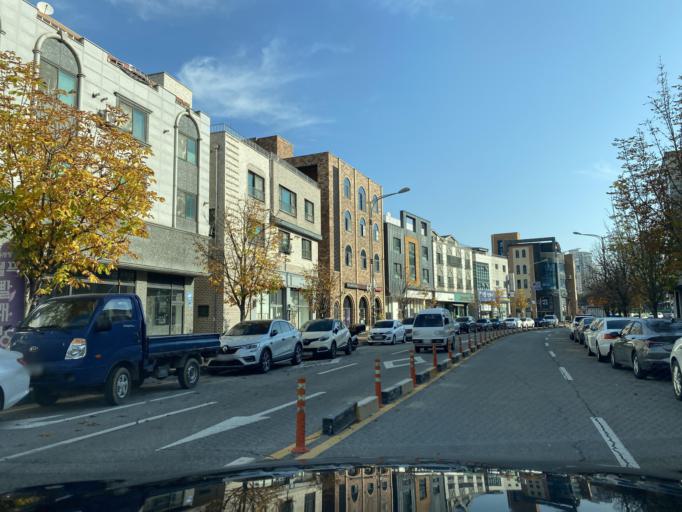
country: KR
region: Chungcheongnam-do
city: Cheonan
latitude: 36.8001
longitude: 127.1064
